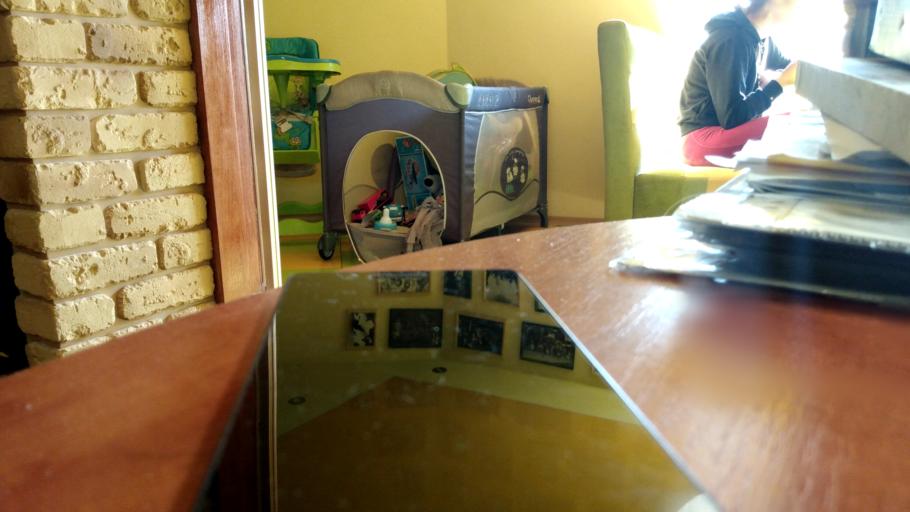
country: RU
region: Penza
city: Serdobsk
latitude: 52.4190
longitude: 44.3142
